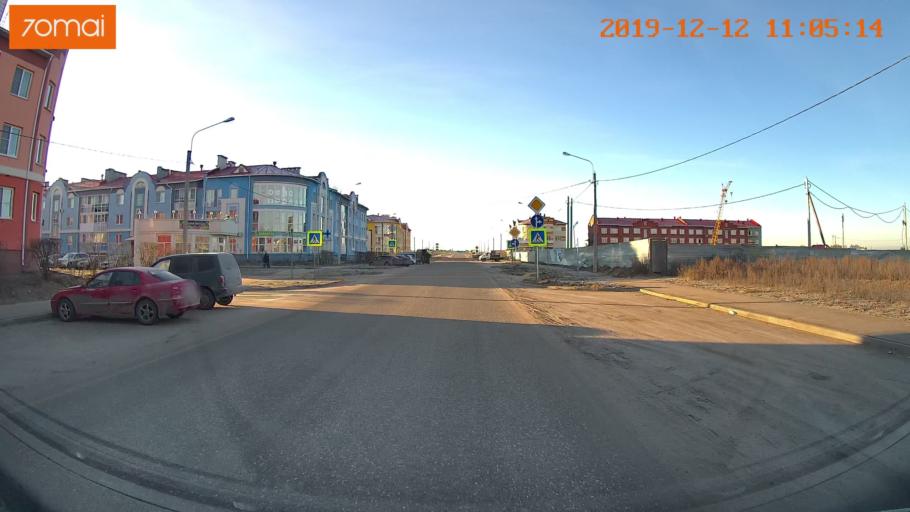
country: RU
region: Ivanovo
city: Kokhma
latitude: 56.9501
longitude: 41.1007
